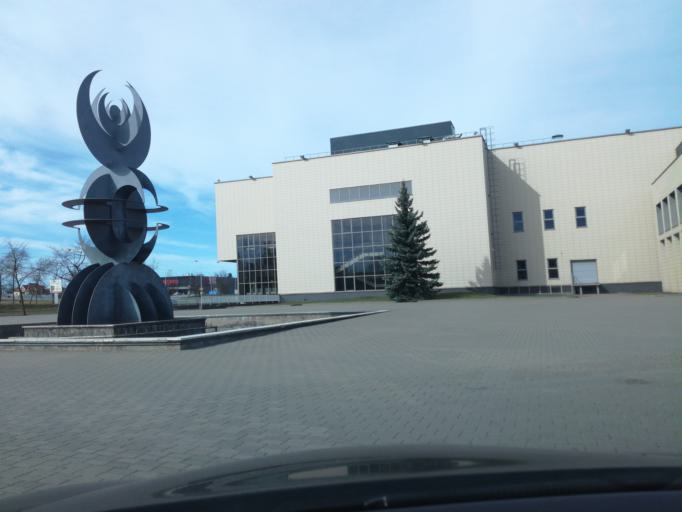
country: LT
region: Alytaus apskritis
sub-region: Alytus
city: Alytus
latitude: 54.4033
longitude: 24.0227
